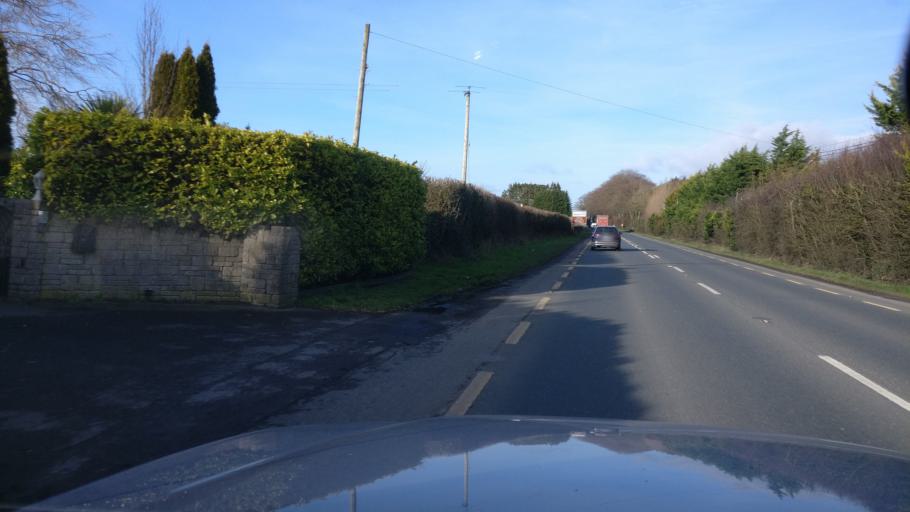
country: IE
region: Leinster
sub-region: Uibh Fhaili
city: Tullamore
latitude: 53.2495
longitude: -7.4773
